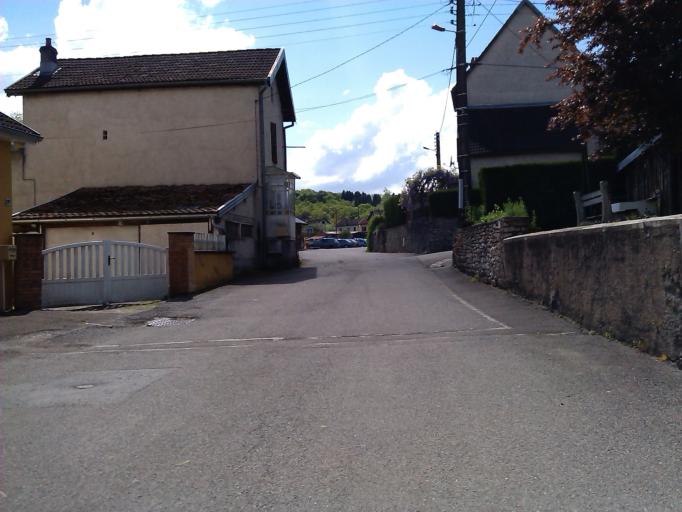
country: FR
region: Franche-Comte
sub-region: Departement du Doubs
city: Bavans
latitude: 47.4747
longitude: 6.7332
